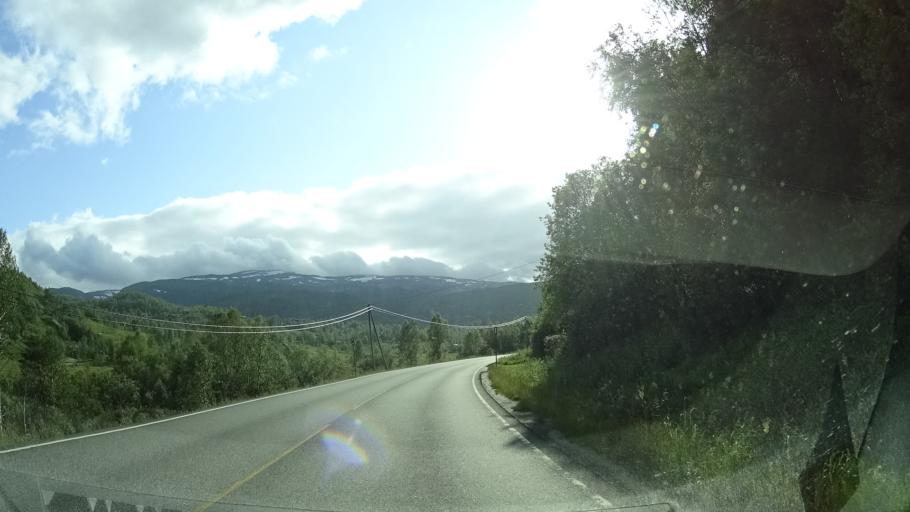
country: NO
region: Hordaland
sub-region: Kvam
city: Norheimsund
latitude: 60.3719
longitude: 5.9996
